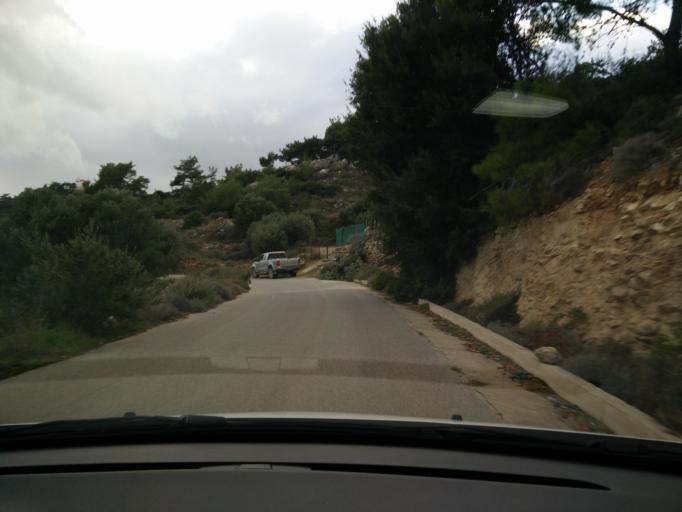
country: GR
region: Crete
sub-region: Nomos Lasithiou
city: Kritsa
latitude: 35.0981
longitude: 25.6913
